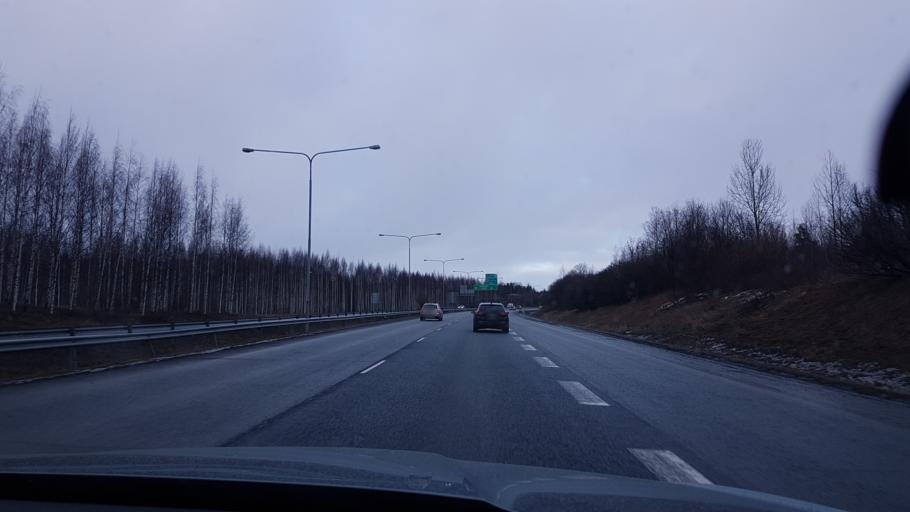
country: FI
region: Pirkanmaa
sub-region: Tampere
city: Tampere
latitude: 61.4897
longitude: 23.8749
